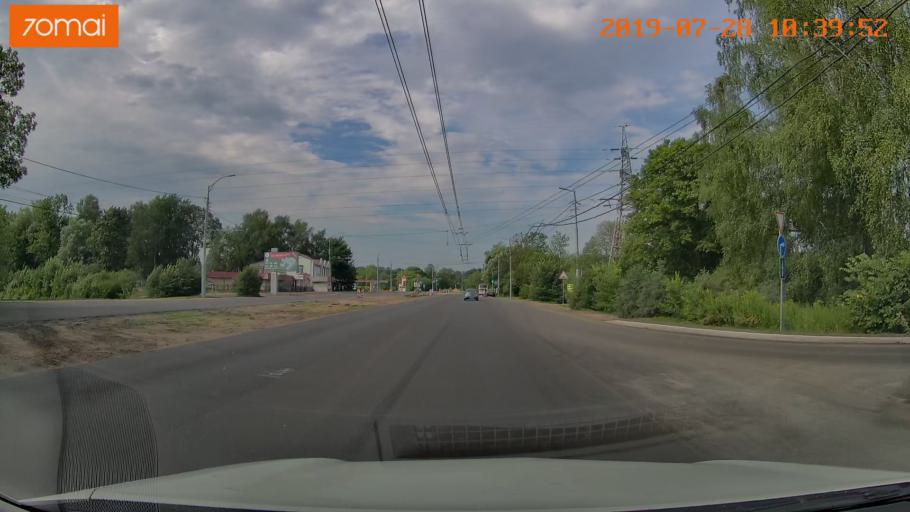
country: RU
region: Kaliningrad
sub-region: Gorod Kaliningrad
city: Kaliningrad
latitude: 54.7163
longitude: 20.3780
